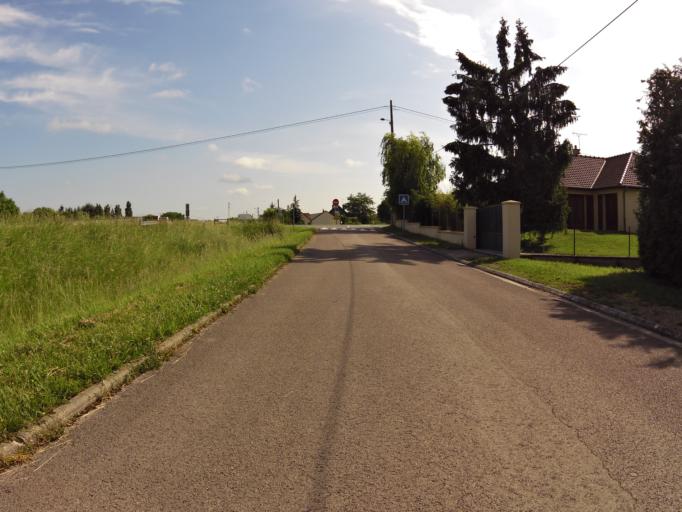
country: FR
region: Champagne-Ardenne
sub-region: Departement de l'Aube
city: Verrieres
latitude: 48.2671
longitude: 4.1377
